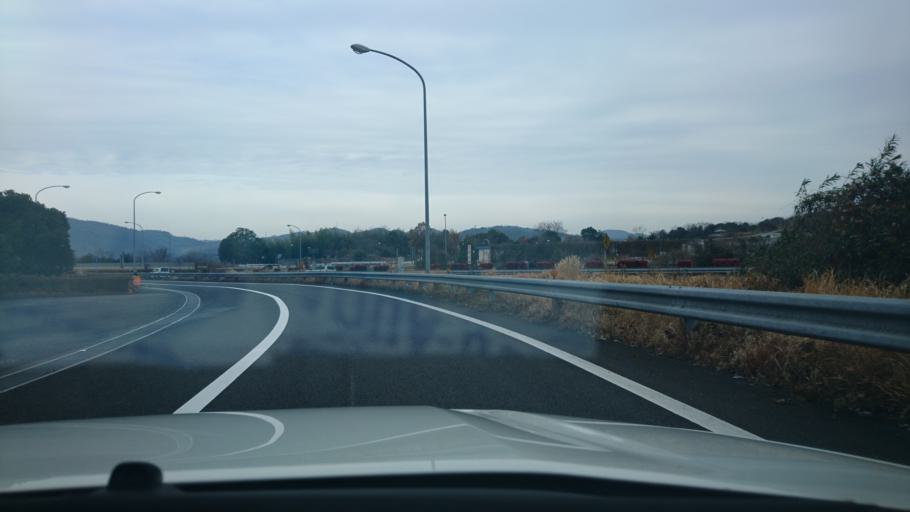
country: JP
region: Okayama
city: Okayama-shi
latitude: 34.6929
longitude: 133.8719
